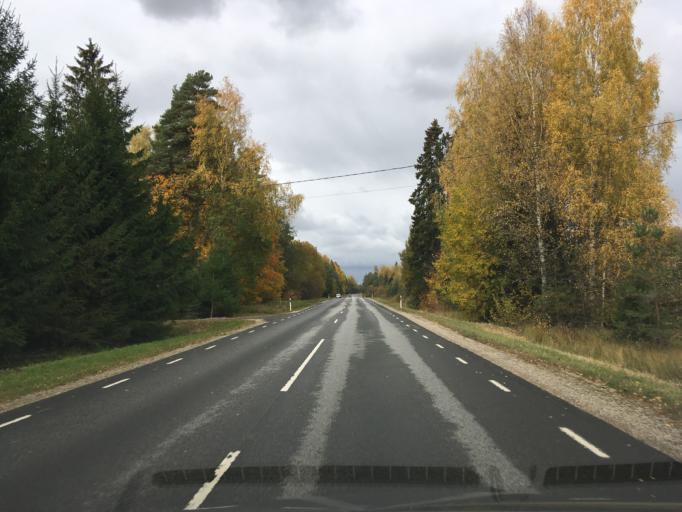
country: EE
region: Harju
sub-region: Anija vald
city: Kehra
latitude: 59.2953
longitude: 25.3720
